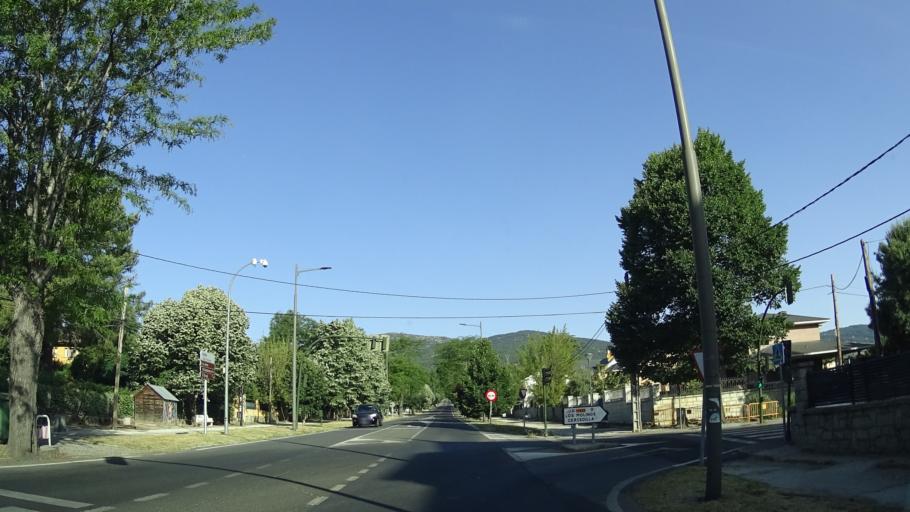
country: ES
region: Madrid
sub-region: Provincia de Madrid
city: Guadarrama
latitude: 40.6753
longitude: -4.0947
